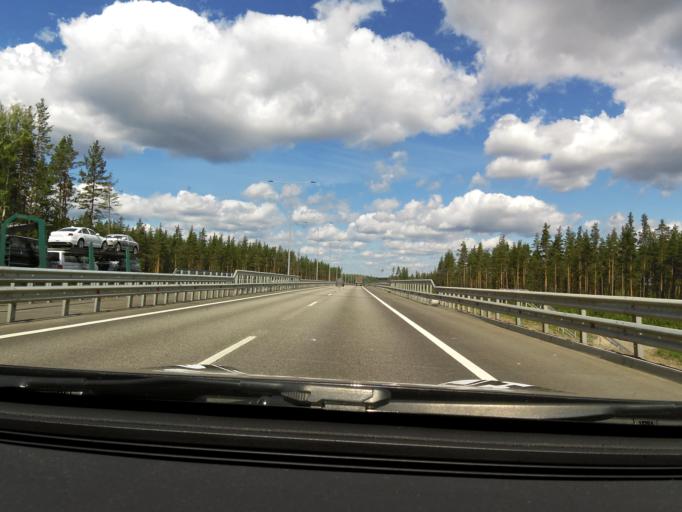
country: RU
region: Tverskaya
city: Krasnomayskiy
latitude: 57.5130
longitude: 34.2852
